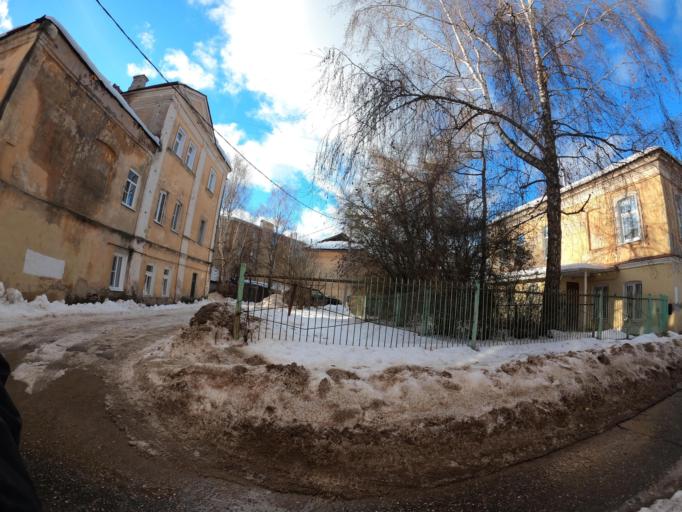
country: RU
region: Kaluga
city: Kaluga
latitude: 54.5090
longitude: 36.2552
